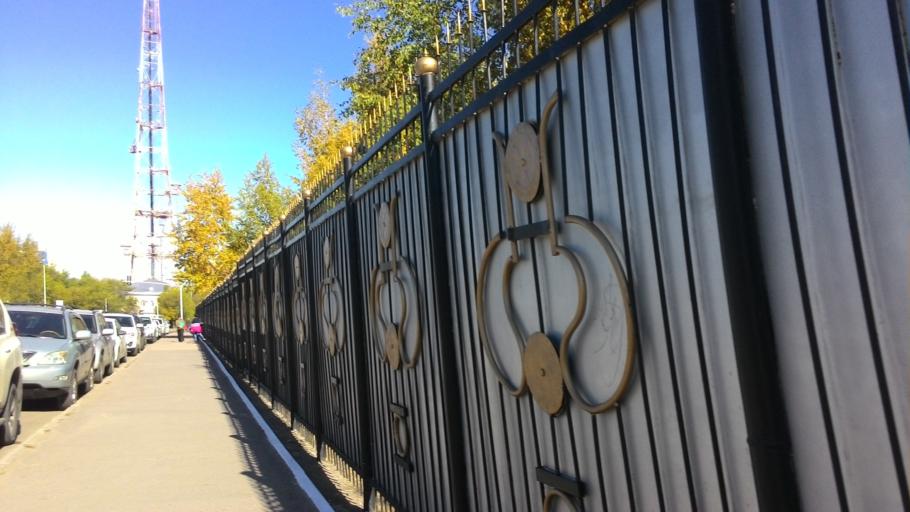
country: KZ
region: Astana Qalasy
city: Astana
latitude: 51.1811
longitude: 71.4122
